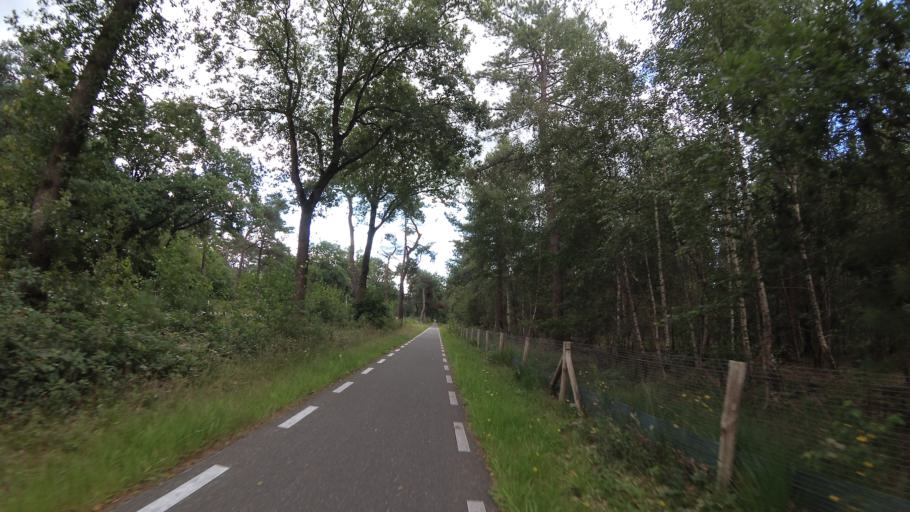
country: NL
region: North Brabant
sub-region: Gemeente Dongen
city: Dongen
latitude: 51.5932
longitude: 4.8994
